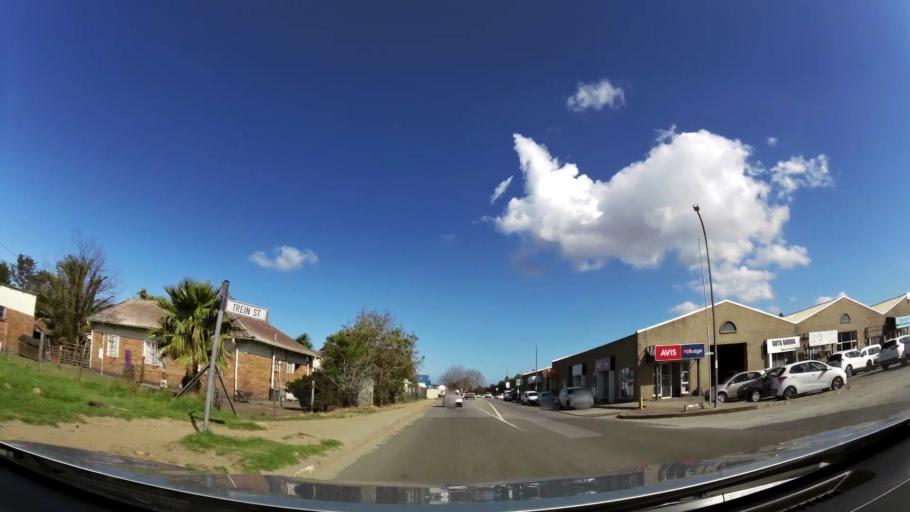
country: ZA
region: Western Cape
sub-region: Eden District Municipality
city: George
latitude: -33.9653
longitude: 22.4670
